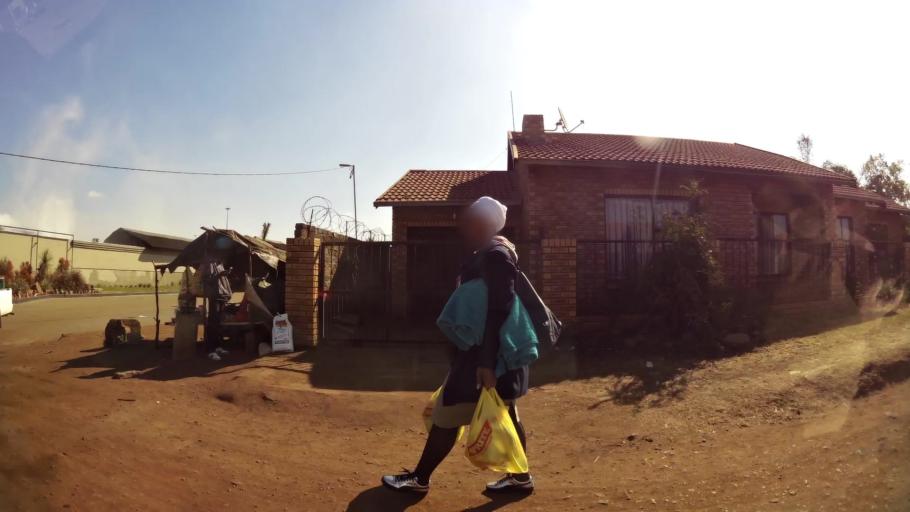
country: ZA
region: Gauteng
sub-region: City of Johannesburg Metropolitan Municipality
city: Soweto
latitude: -26.2899
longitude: 27.8543
